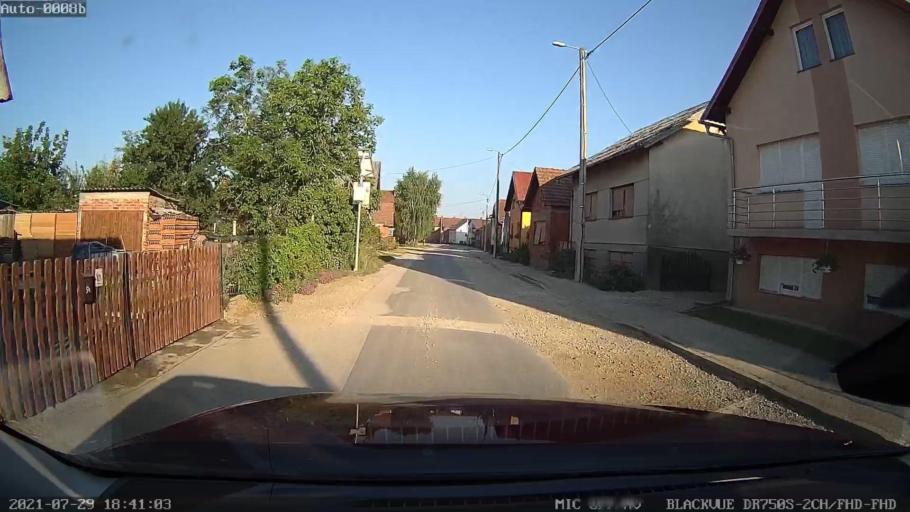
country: HR
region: Varazdinska
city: Petrijanec
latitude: 46.3185
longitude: 16.2324
